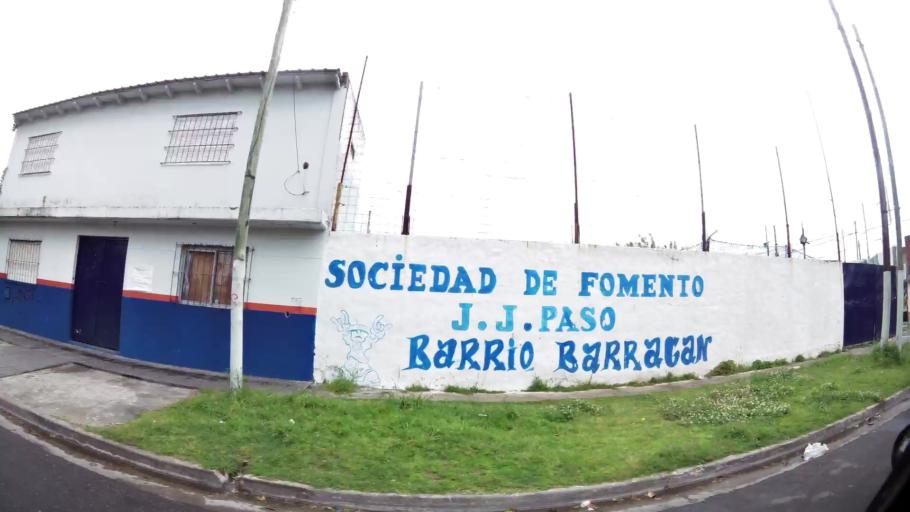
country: AR
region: Buenos Aires
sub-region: Partido de Quilmes
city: Quilmes
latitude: -34.7618
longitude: -58.1982
